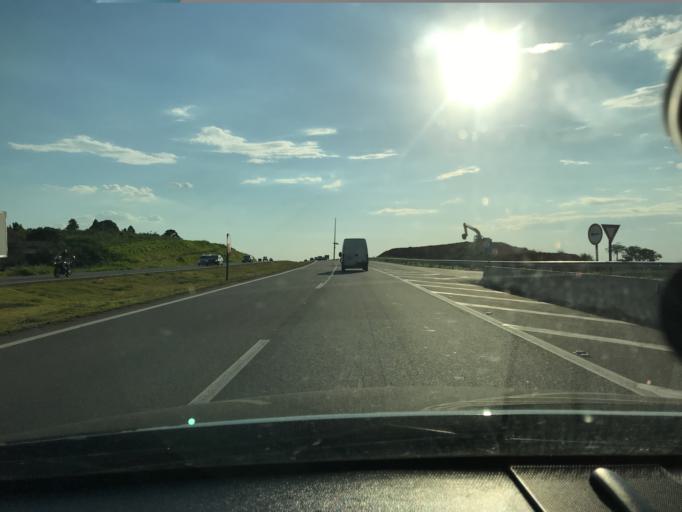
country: BR
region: Sao Paulo
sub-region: Valinhos
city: Valinhos
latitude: -22.9914
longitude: -47.0687
